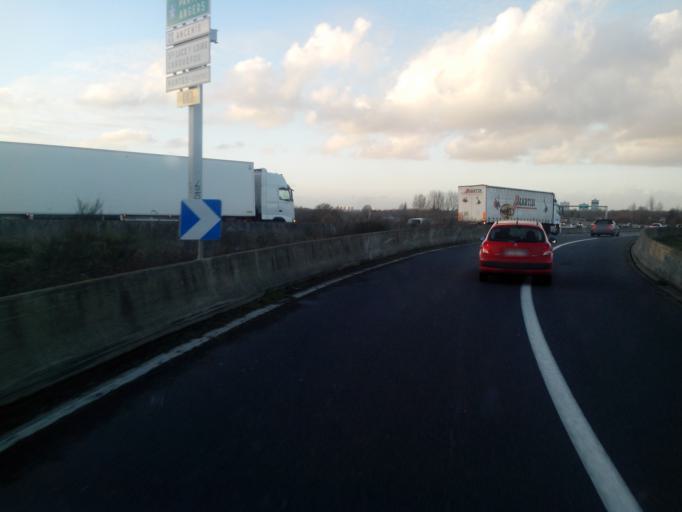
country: FR
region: Pays de la Loire
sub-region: Departement de la Loire-Atlantique
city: Basse-Goulaine
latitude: 47.2283
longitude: -1.4683
